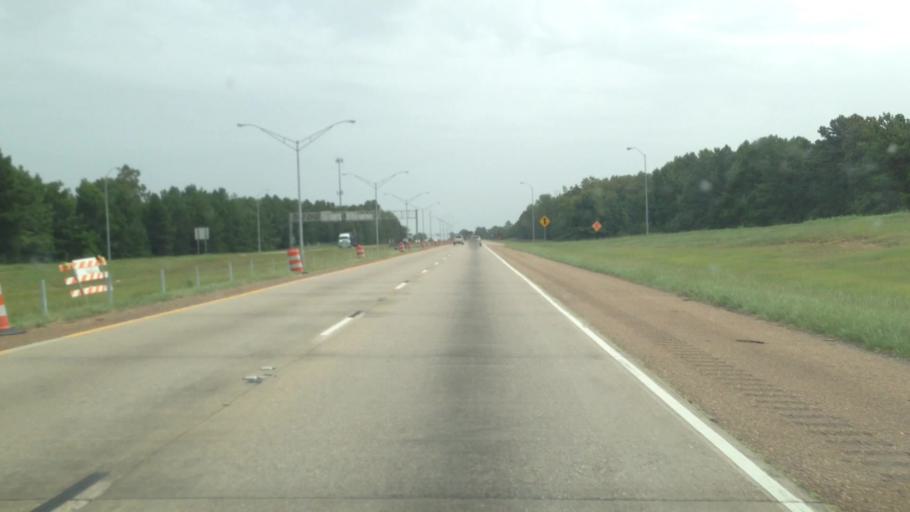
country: US
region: Louisiana
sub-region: Caddo Parish
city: Shreveport
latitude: 32.4864
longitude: -93.8274
